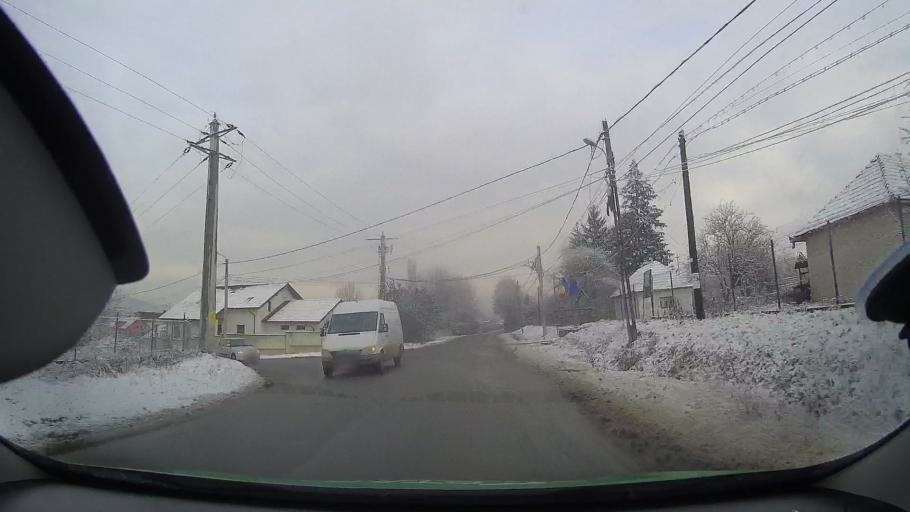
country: RO
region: Mures
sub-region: Comuna Bogata
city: Bogata
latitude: 46.4618
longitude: 24.0816
